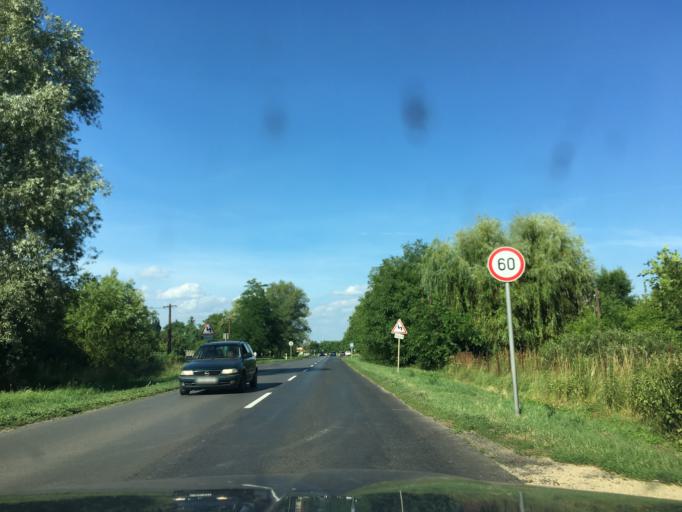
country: HU
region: Hajdu-Bihar
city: Hajdusamson
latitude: 47.5775
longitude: 21.7084
